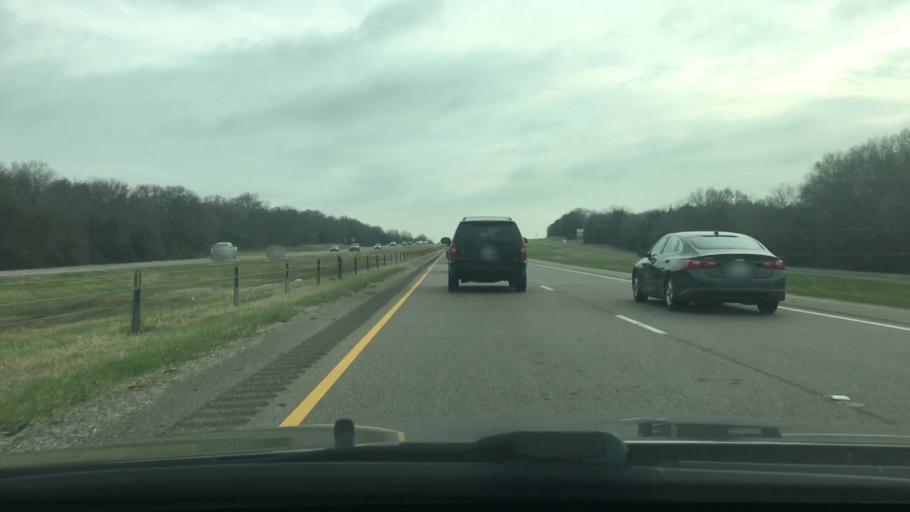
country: US
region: Texas
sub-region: Freestone County
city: Fairfield
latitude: 31.6459
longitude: -96.1594
